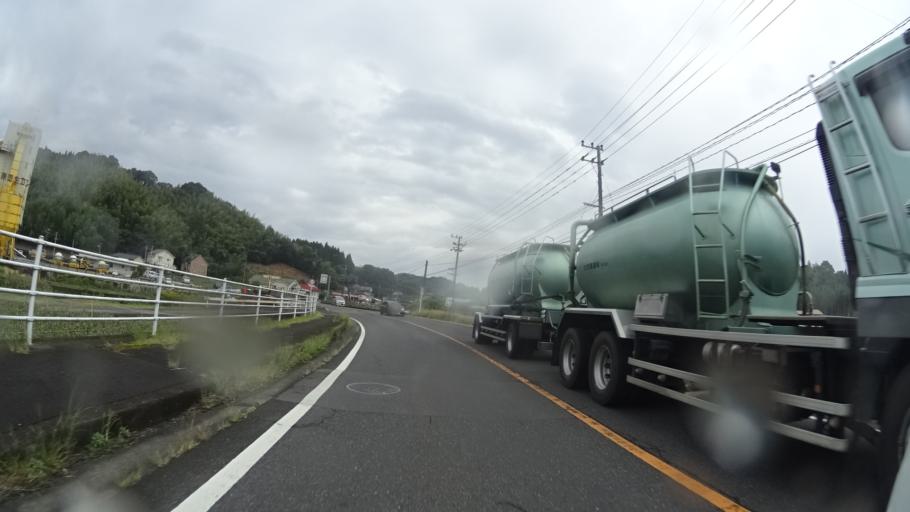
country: JP
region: Kagoshima
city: Kajiki
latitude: 31.7571
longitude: 130.6765
